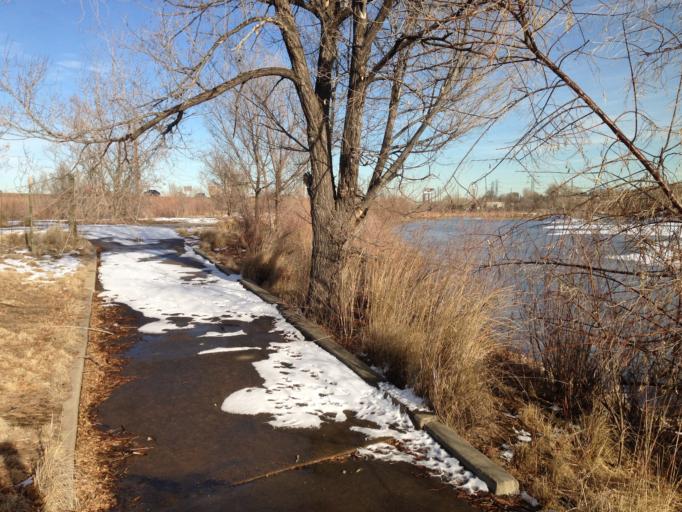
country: US
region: Colorado
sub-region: Adams County
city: Berkley
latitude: 39.7984
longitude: -105.0395
